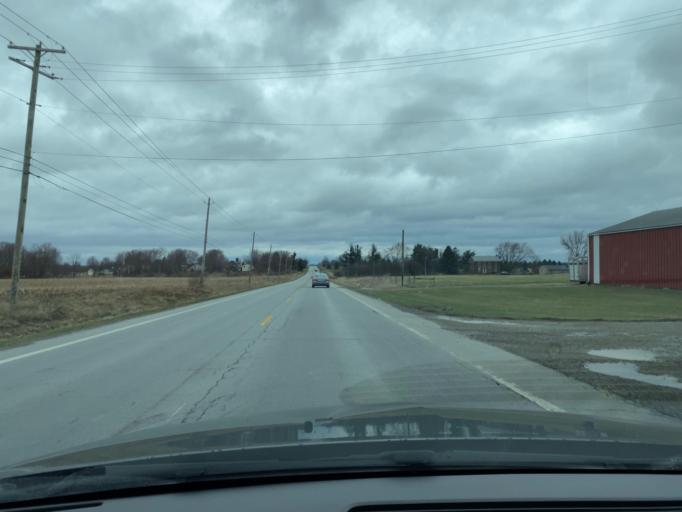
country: US
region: Ohio
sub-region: Wayne County
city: Orrville
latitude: 40.8915
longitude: -81.7630
